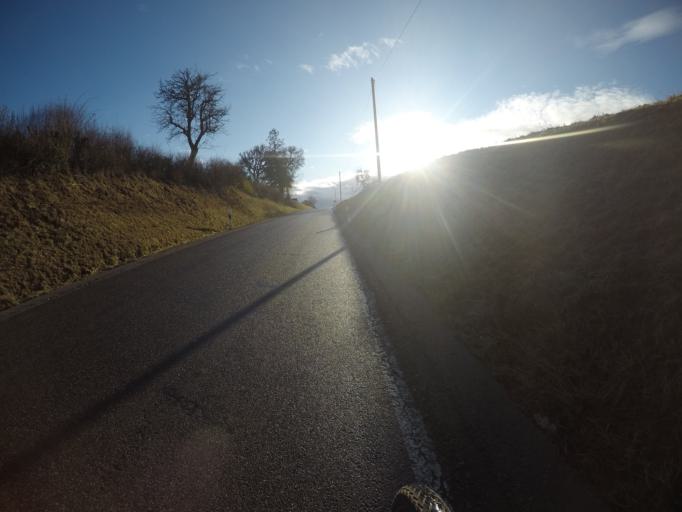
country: DE
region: Baden-Wuerttemberg
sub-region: Regierungsbezirk Stuttgart
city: Bondorf
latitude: 48.5326
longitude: 8.8747
